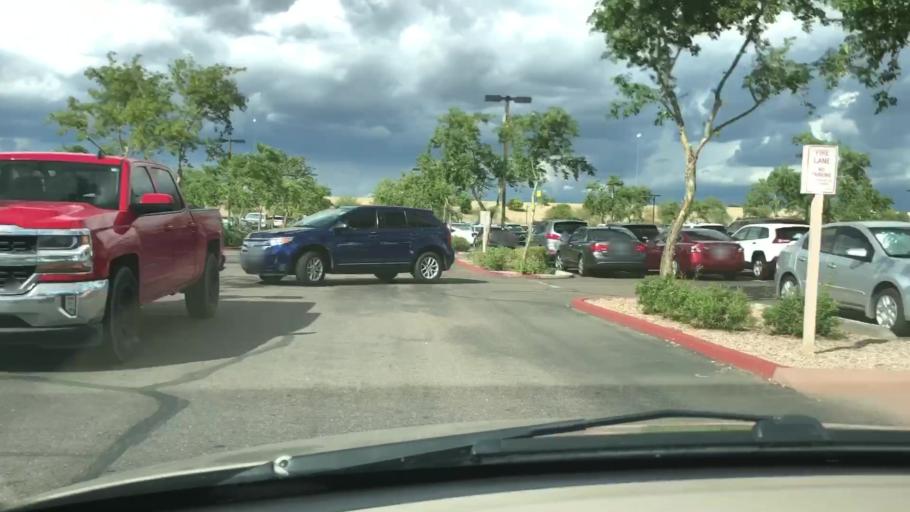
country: US
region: Arizona
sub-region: Maricopa County
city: Peoria
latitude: 33.6664
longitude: -112.1287
